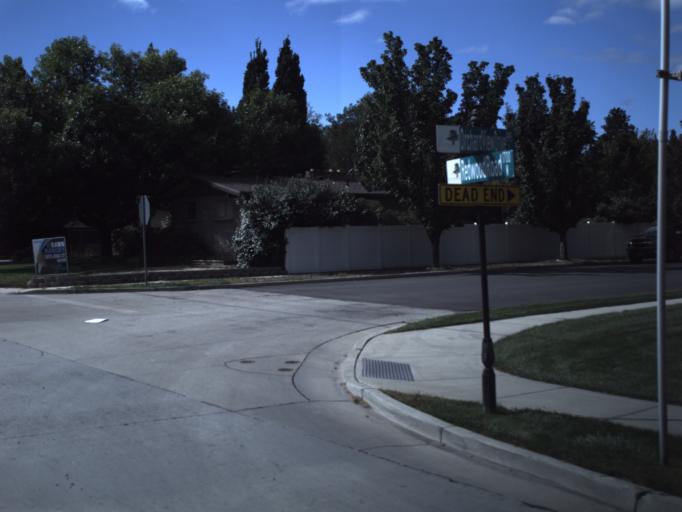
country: US
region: Utah
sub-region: Salt Lake County
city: South Jordan
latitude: 40.5698
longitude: -111.9388
